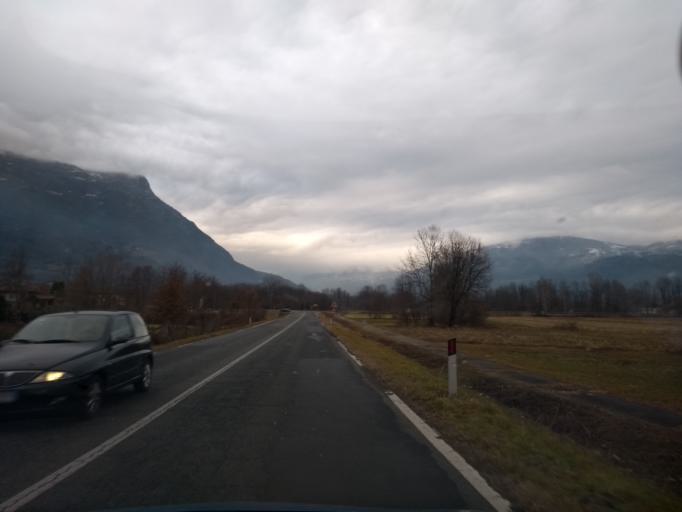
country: IT
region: Piedmont
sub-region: Provincia di Torino
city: Fiorano Canavese
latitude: 45.4812
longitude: 7.8307
